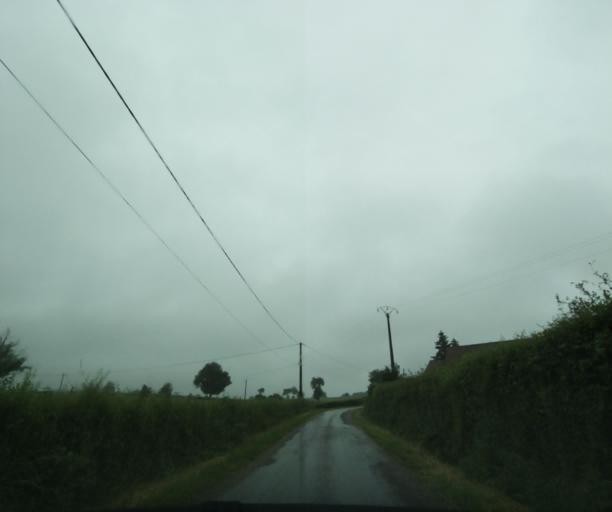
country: FR
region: Bourgogne
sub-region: Departement de Saone-et-Loire
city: Charolles
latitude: 46.4111
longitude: 4.2400
